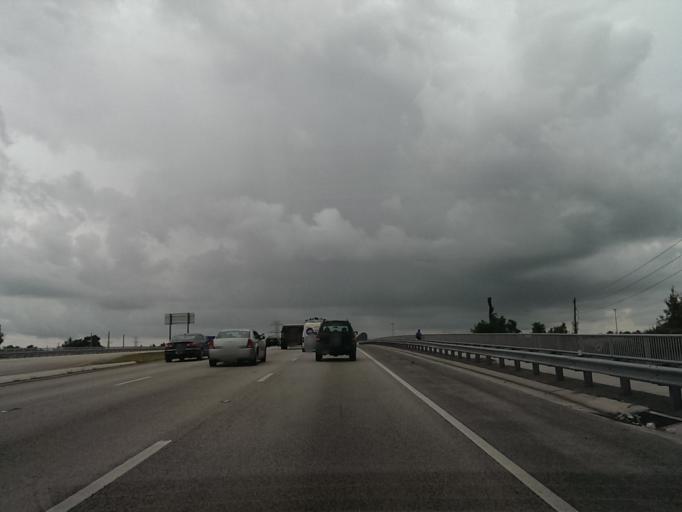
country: US
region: Florida
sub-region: Orange County
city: Tangelo Park
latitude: 28.4915
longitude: -81.4588
